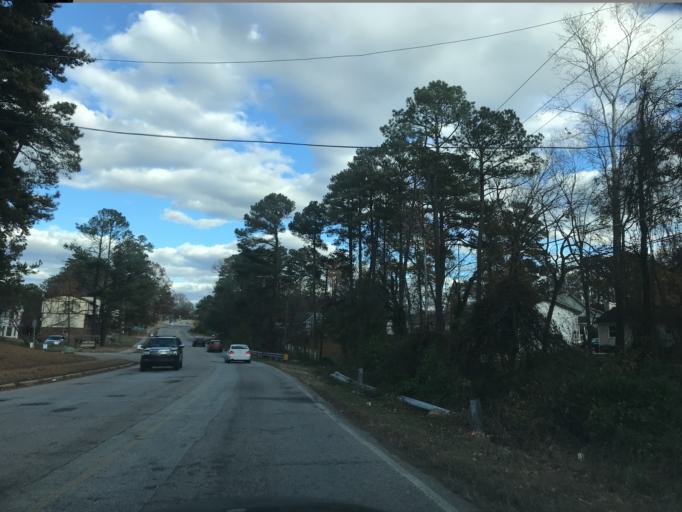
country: US
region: North Carolina
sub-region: Wake County
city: Raleigh
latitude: 35.8357
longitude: -78.5891
